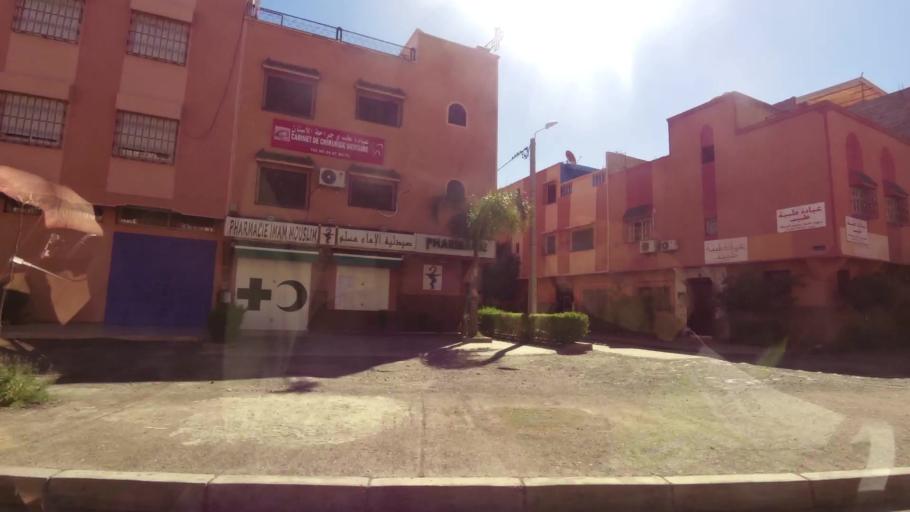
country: MA
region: Marrakech-Tensift-Al Haouz
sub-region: Marrakech
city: Marrakesh
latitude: 31.5935
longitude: -8.0464
